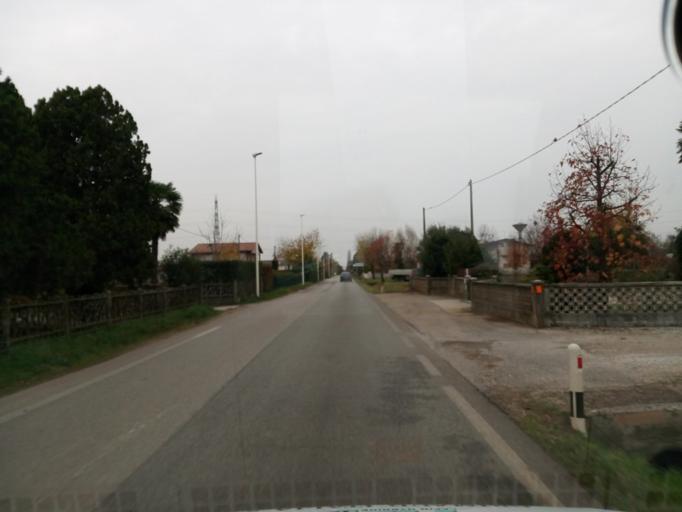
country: IT
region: Veneto
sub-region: Provincia di Treviso
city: Fanzolo
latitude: 45.7222
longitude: 12.0197
